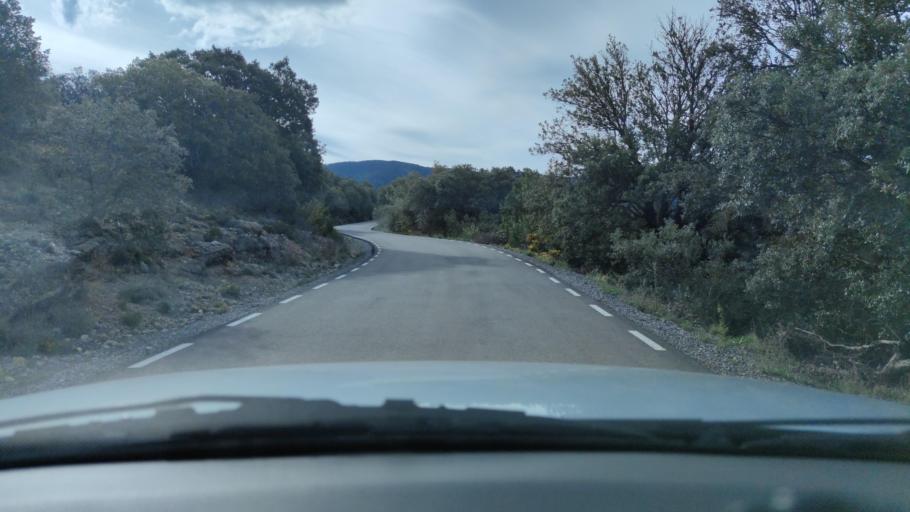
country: ES
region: Catalonia
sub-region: Provincia de Lleida
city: Coll de Nargo
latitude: 42.2319
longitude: 1.4001
